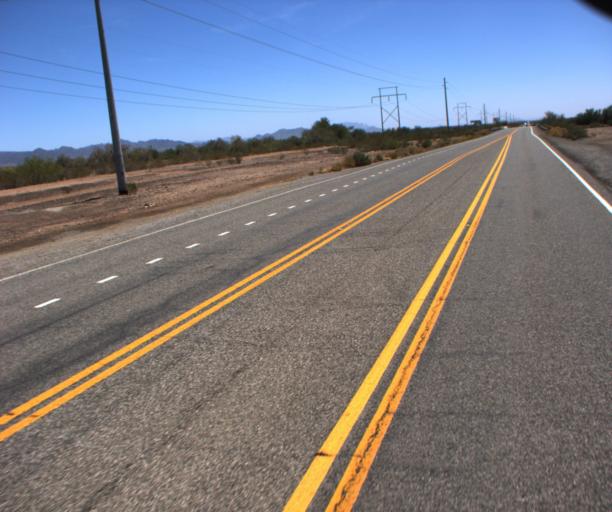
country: US
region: Arizona
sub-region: La Paz County
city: Quartzsite
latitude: 33.7486
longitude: -114.2171
